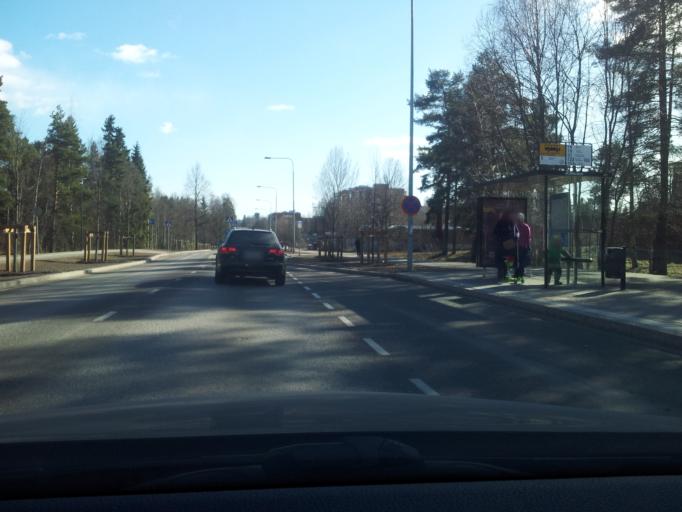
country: FI
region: Uusimaa
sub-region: Helsinki
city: Koukkuniemi
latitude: 60.1716
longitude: 24.7316
